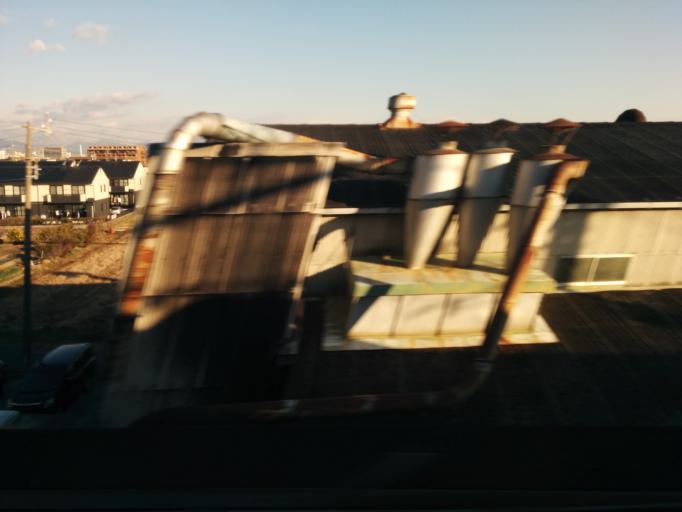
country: JP
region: Gifu
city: Ogaki
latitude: 35.3474
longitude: 136.6112
